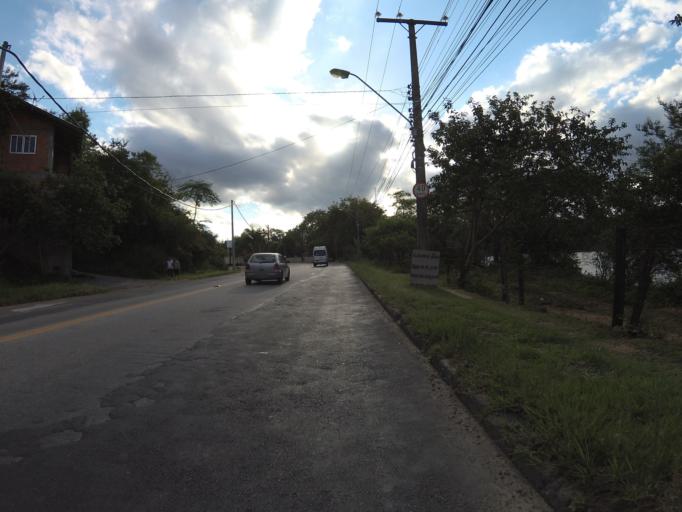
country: BR
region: Santa Catarina
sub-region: Blumenau
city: Blumenau
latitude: -26.8846
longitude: -49.1113
